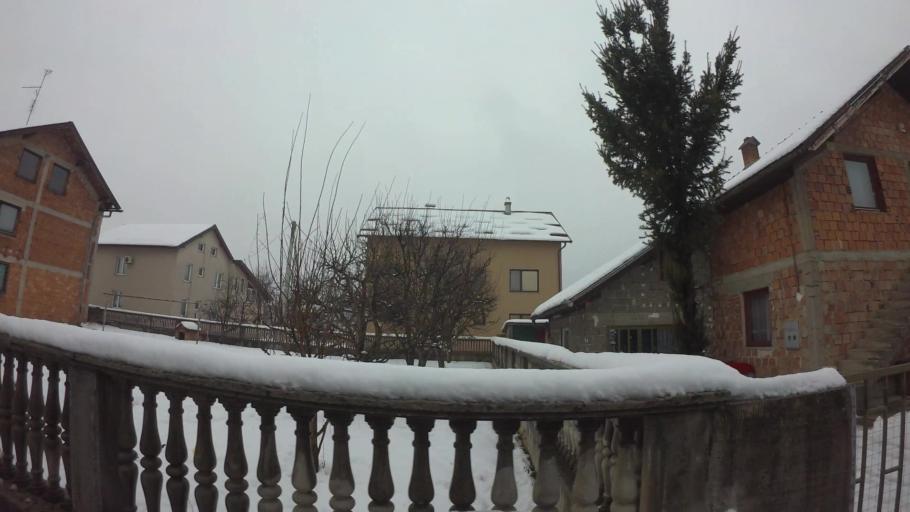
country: BA
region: Federation of Bosnia and Herzegovina
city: Hadzici
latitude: 43.8435
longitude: 18.2768
